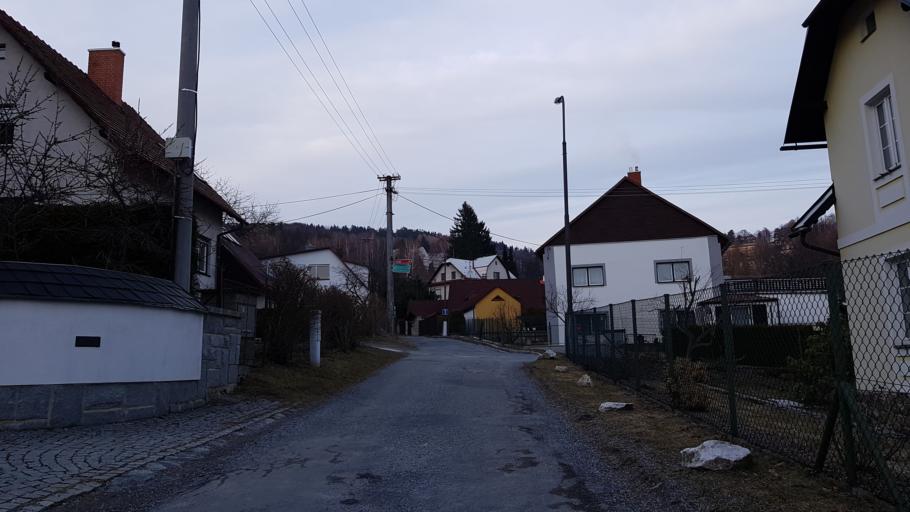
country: CZ
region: Olomoucky
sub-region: Okres Jesenik
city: Jesenik
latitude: 50.2336
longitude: 17.1857
